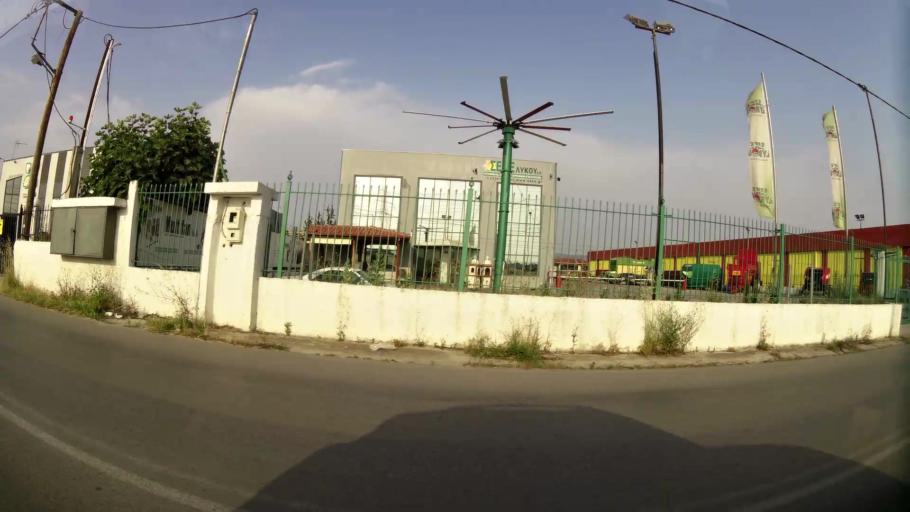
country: GR
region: Central Macedonia
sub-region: Nomos Thessalonikis
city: Oraiokastro
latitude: 40.7032
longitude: 22.9129
